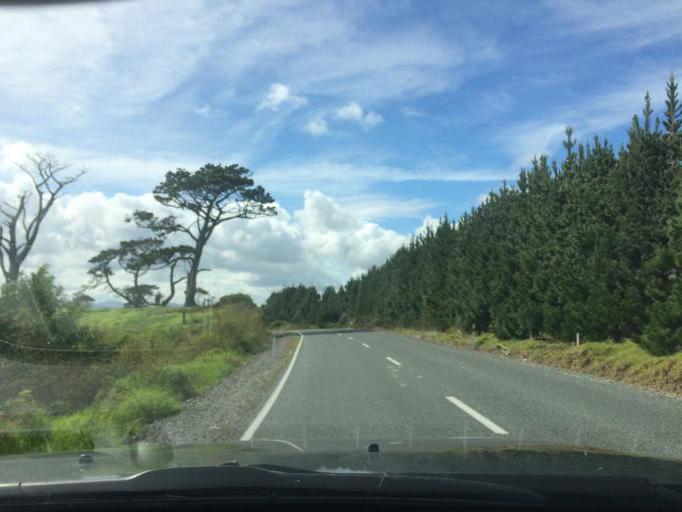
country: NZ
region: Northland
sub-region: Kaipara District
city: Dargaville
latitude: -35.9484
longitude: 173.7680
